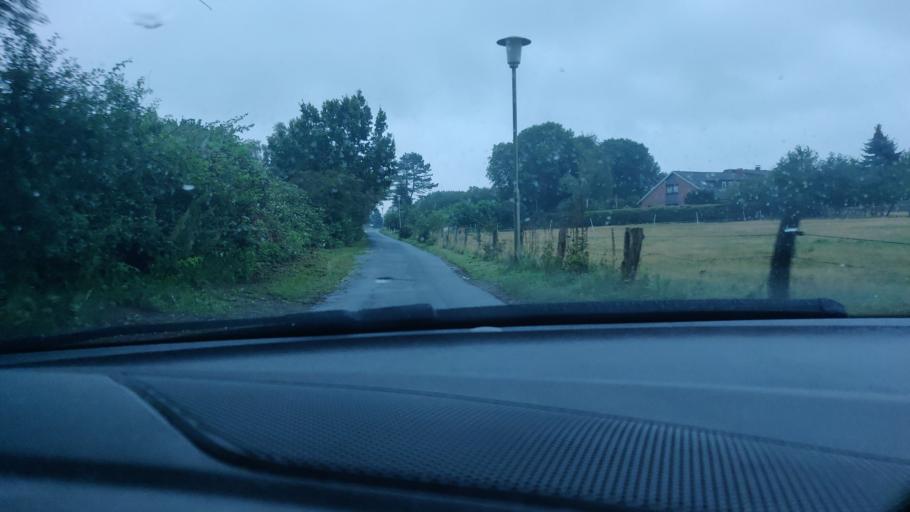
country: DE
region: Lower Saxony
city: Cuxhaven
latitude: 53.8675
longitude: 8.6452
